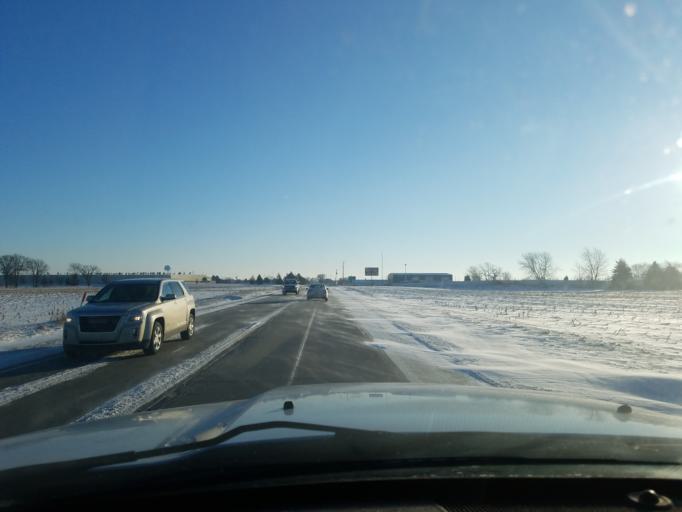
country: US
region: Indiana
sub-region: Noble County
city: Ligonier
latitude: 41.4519
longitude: -85.6100
